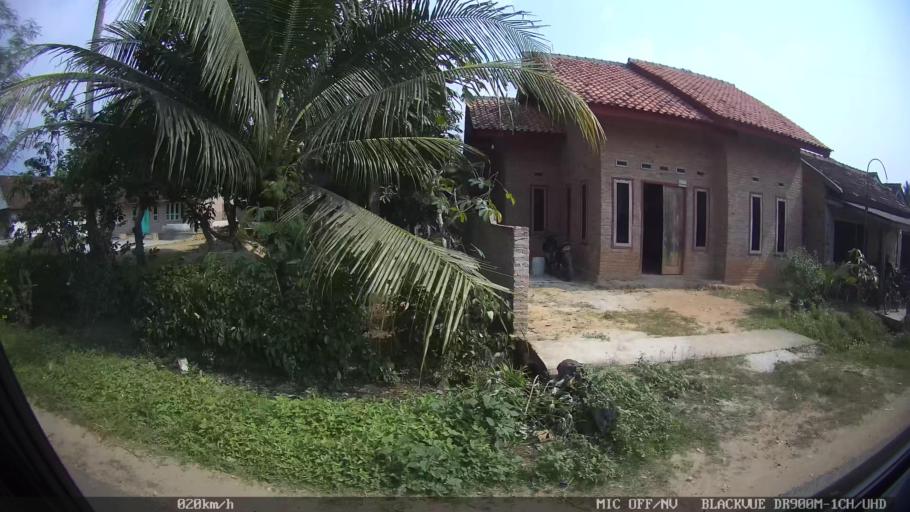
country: ID
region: Lampung
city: Kedondong
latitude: -5.4101
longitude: 104.9979
